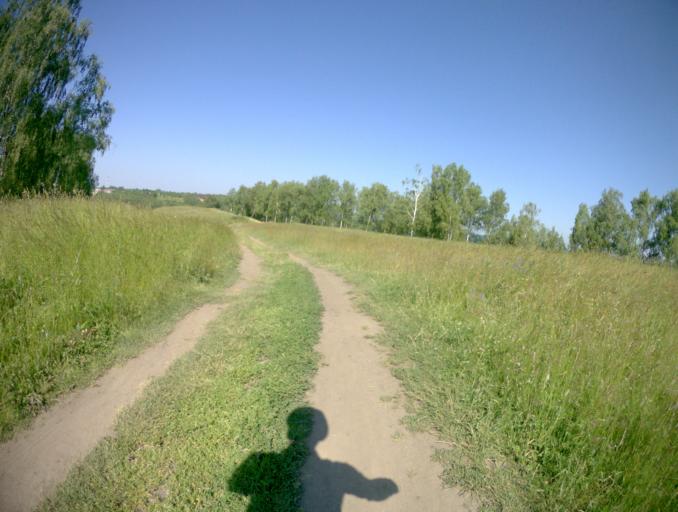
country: RU
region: Vladimir
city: Novovyazniki
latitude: 56.2361
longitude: 42.2446
